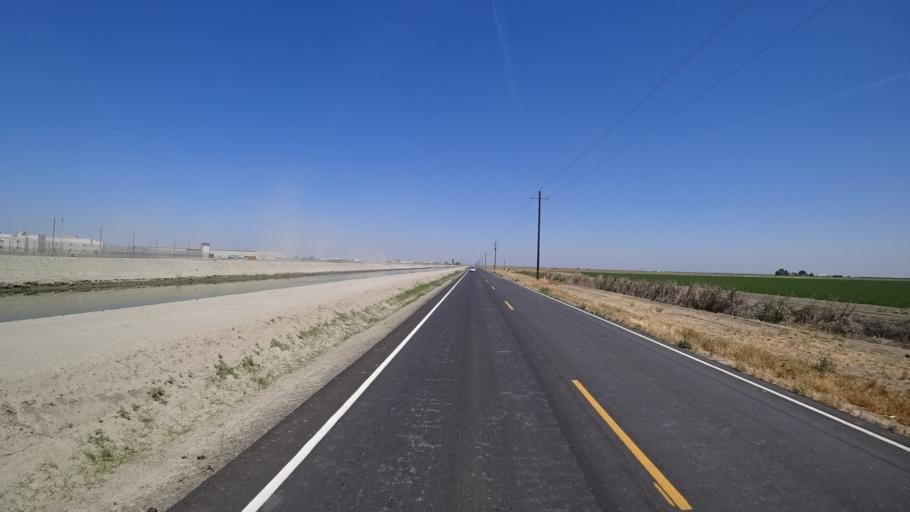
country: US
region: California
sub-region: Kings County
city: Corcoran
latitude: 36.0543
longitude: -119.5363
